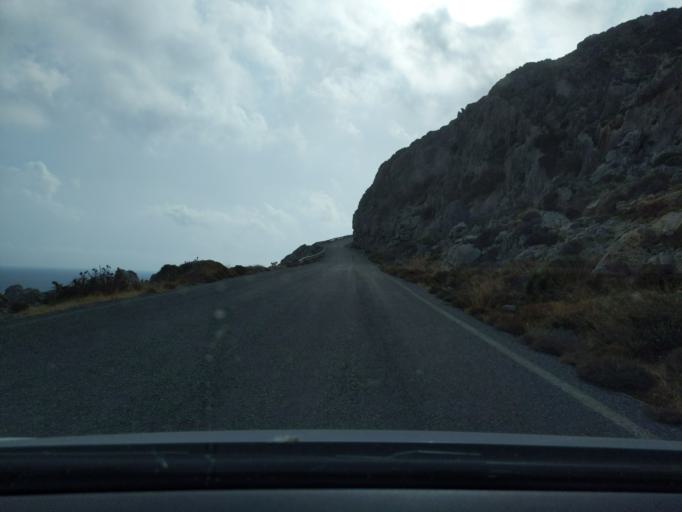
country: GR
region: Crete
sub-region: Nomos Lasithiou
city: Palekastro
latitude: 35.0895
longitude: 26.2653
